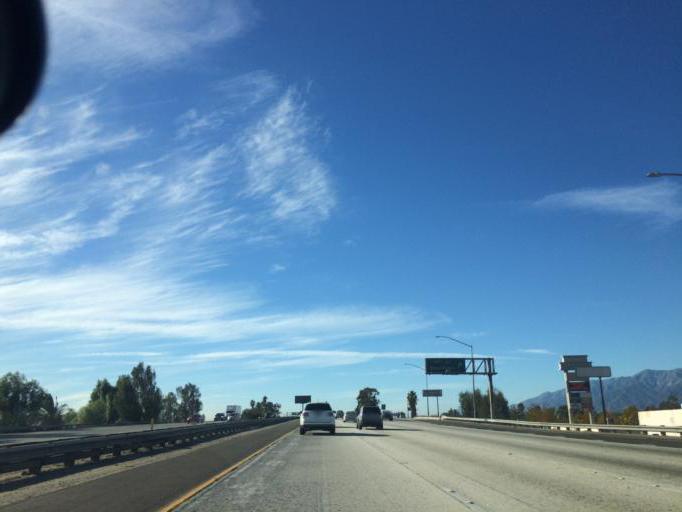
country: US
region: California
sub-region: San Bernardino County
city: Colton
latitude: 34.0654
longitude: -117.3189
